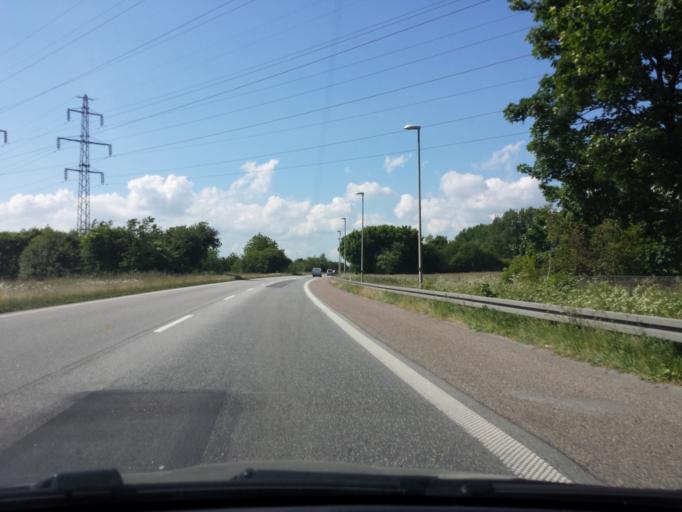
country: DK
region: Capital Region
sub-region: Brondby Kommune
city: Brondbyvester
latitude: 55.6303
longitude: 12.4318
